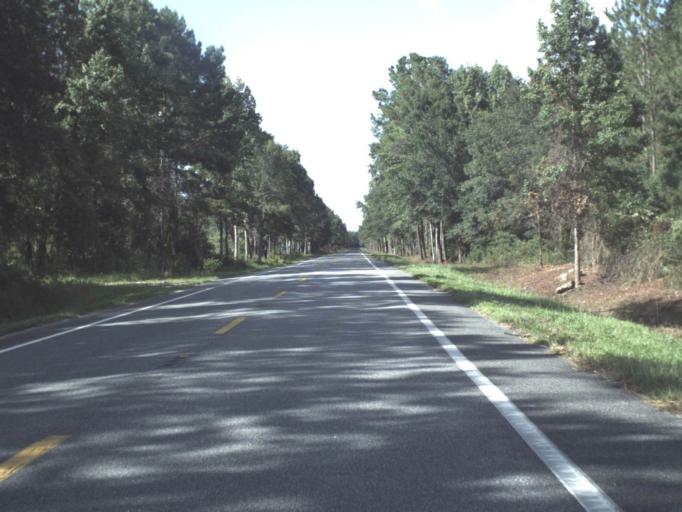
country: US
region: Florida
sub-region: Lafayette County
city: Mayo
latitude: 29.9043
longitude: -83.2940
